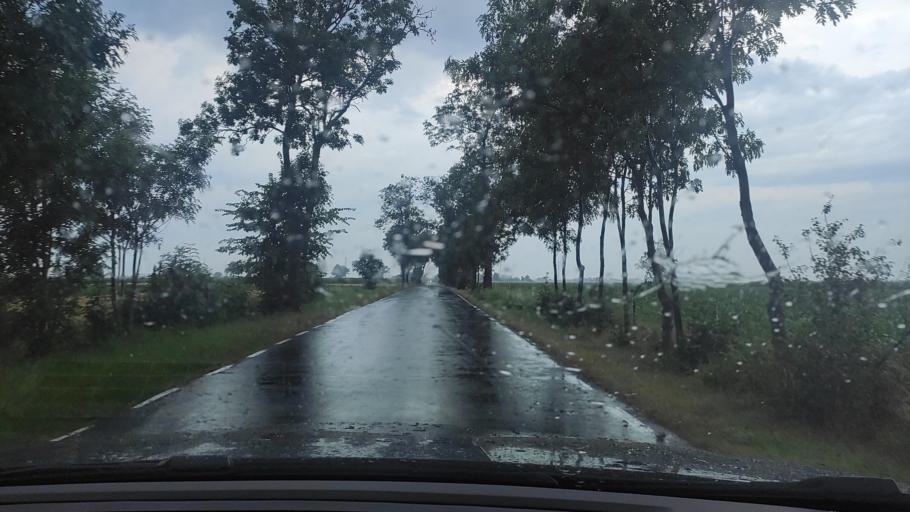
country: PL
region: Greater Poland Voivodeship
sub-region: Powiat poznanski
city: Kleszczewo
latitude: 52.2906
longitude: 17.1810
